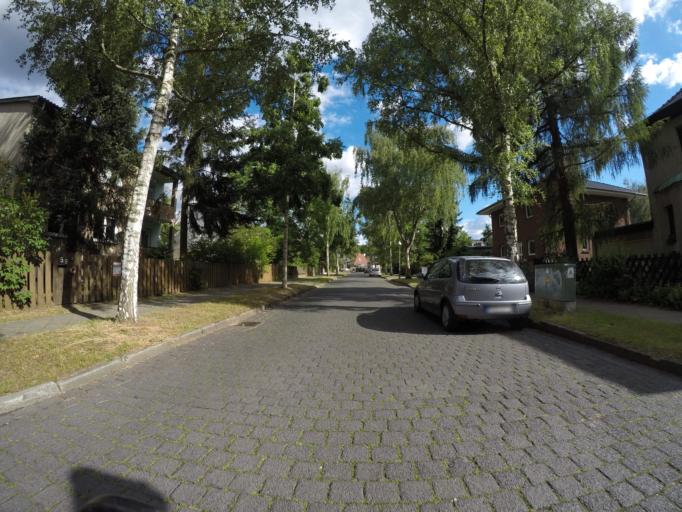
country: DE
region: Berlin
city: Zehlendorf Bezirk
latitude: 52.4260
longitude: 13.2677
